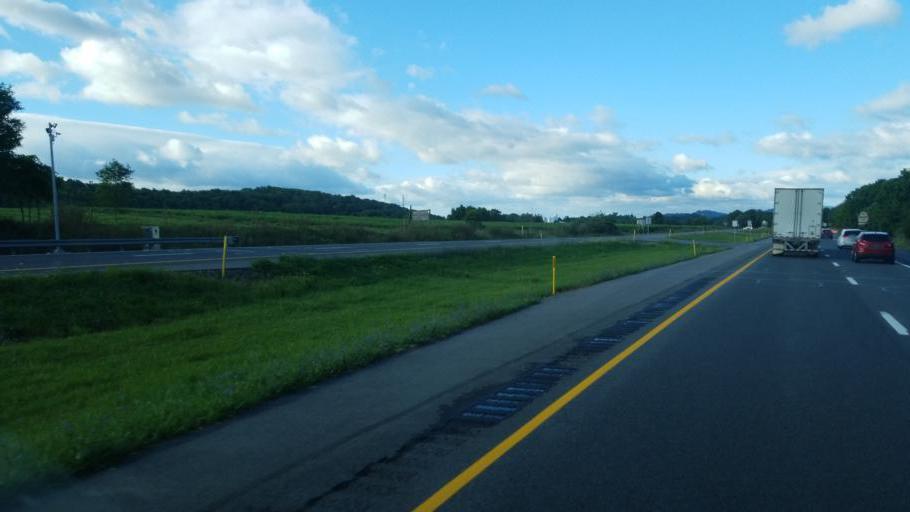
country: US
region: Maryland
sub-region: Washington County
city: Hancock
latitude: 39.7239
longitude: -78.1839
